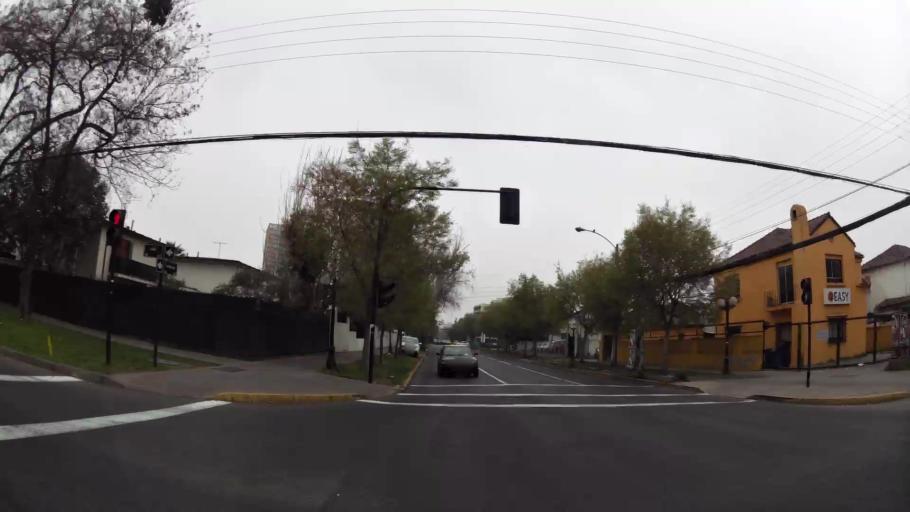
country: CL
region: Santiago Metropolitan
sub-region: Provincia de Santiago
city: Santiago
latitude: -33.4379
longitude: -70.6141
